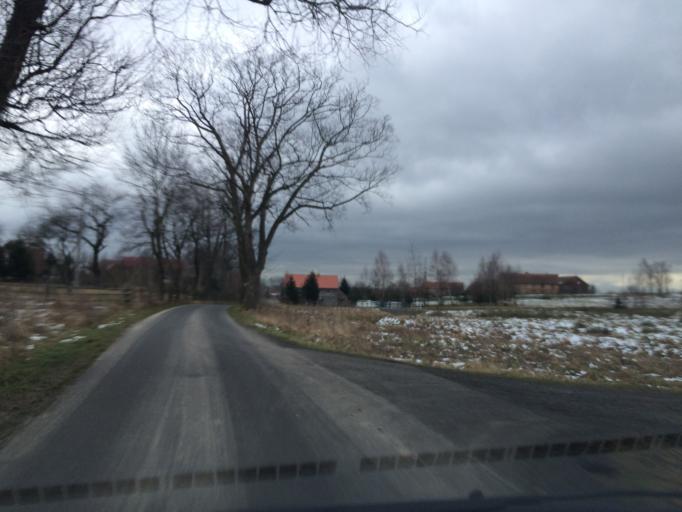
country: PL
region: Lower Silesian Voivodeship
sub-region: Powiat lubanski
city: Pisarzowice
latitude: 51.1706
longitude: 15.2239
